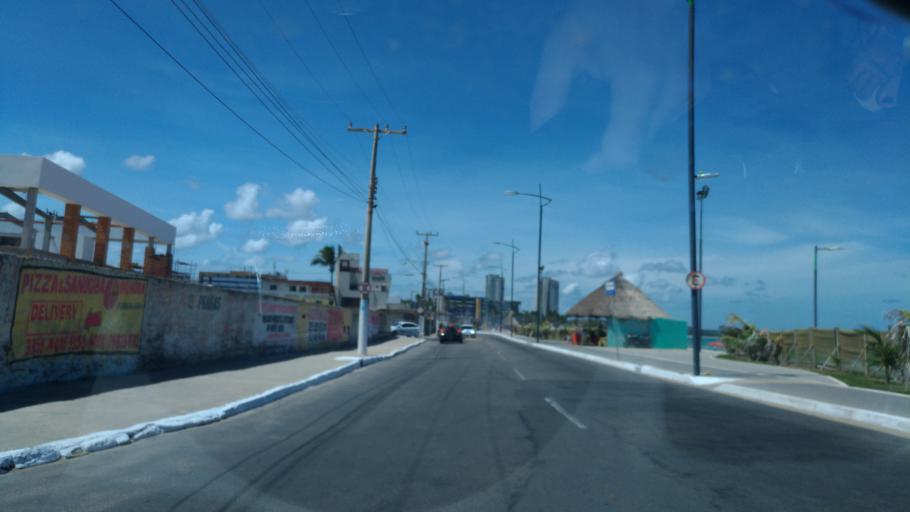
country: BR
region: Alagoas
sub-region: Maceio
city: Maceio
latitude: -9.6385
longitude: -35.6983
